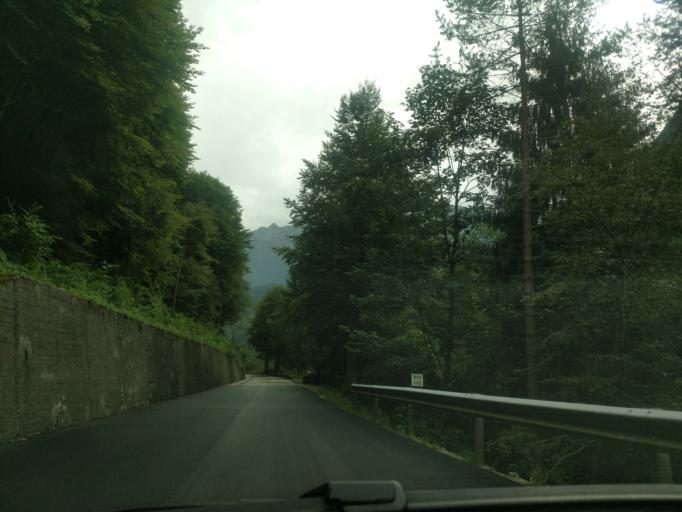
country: IT
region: Veneto
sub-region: Provincia di Belluno
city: Longarone
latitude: 46.2846
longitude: 12.2409
